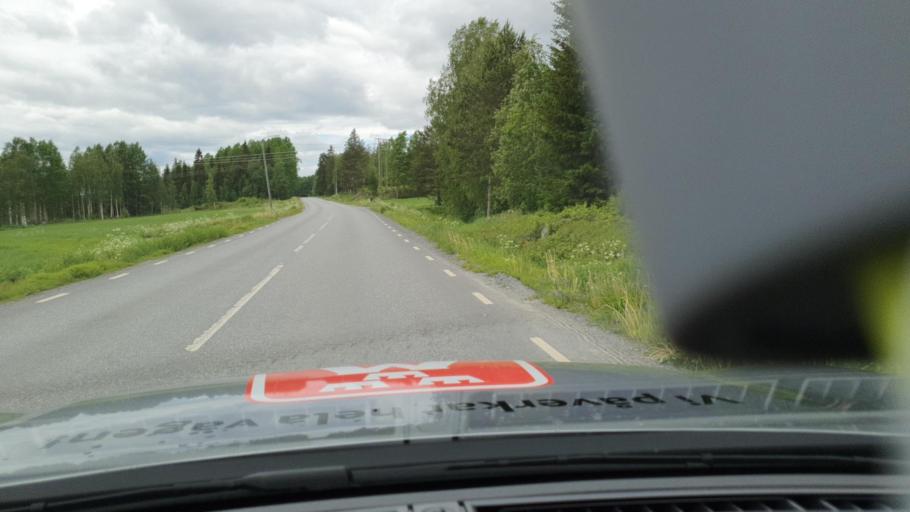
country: SE
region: Norrbotten
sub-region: Lulea Kommun
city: Sodra Sunderbyn
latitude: 65.8247
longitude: 21.9804
